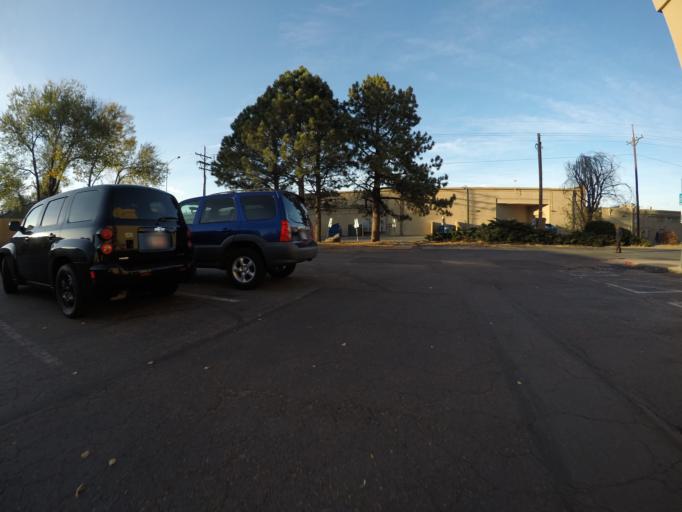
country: US
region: Colorado
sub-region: Boulder County
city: Boulder
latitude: 40.0128
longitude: -105.2618
